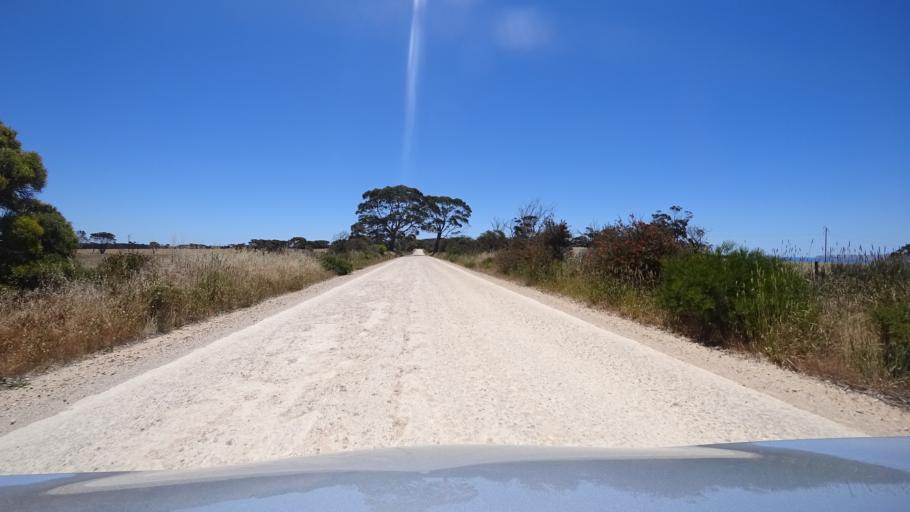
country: AU
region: South Australia
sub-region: Kangaroo Island
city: Kingscote
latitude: -35.7424
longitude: 138.0075
